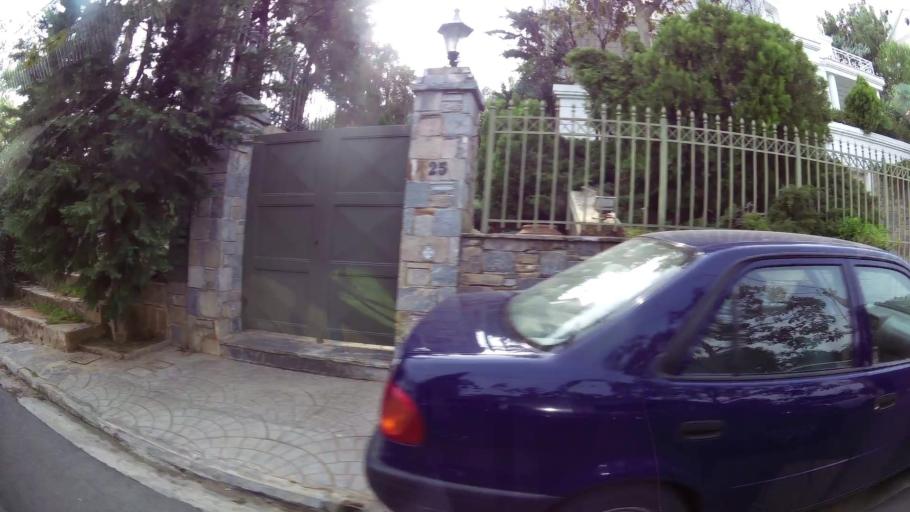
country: GR
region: Attica
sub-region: Nomarchia Athinas
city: Filothei
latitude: 38.0265
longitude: 23.7722
